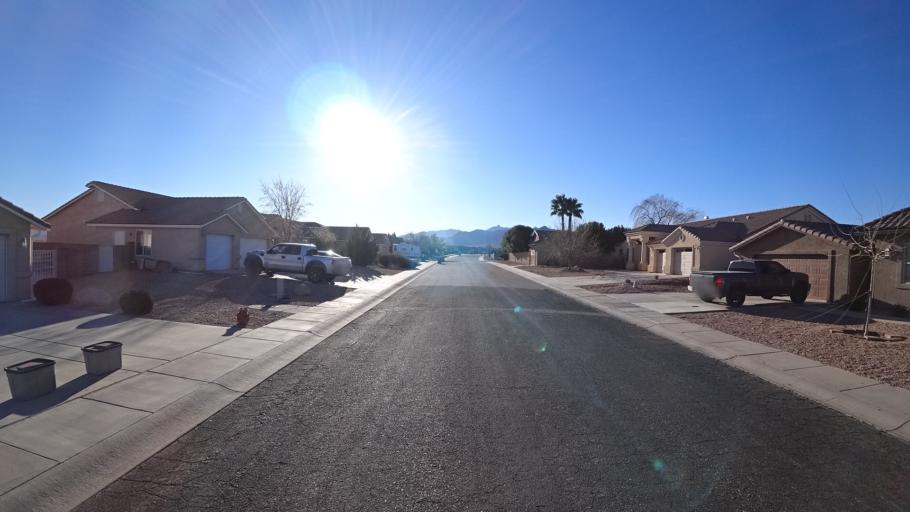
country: US
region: Arizona
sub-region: Mohave County
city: New Kingman-Butler
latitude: 35.2217
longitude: -113.9720
